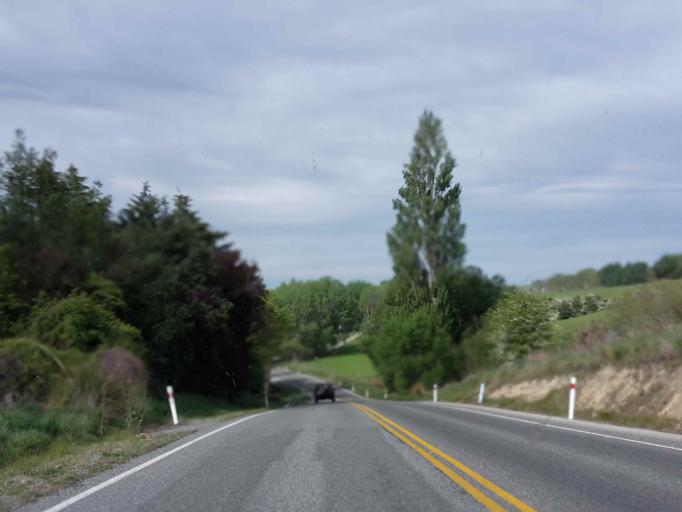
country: NZ
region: Canterbury
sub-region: Timaru District
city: Pleasant Point
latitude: -44.1185
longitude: 171.1284
